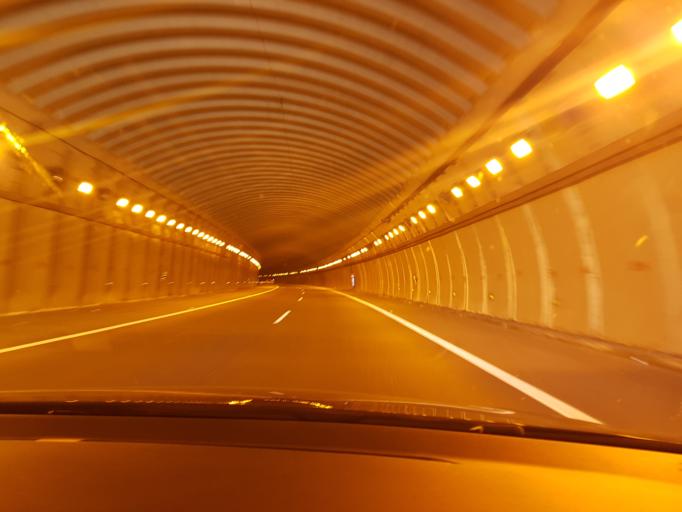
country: ES
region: Andalusia
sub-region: Provincia de Malaga
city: Fuengirola
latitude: 36.5069
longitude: -4.7249
